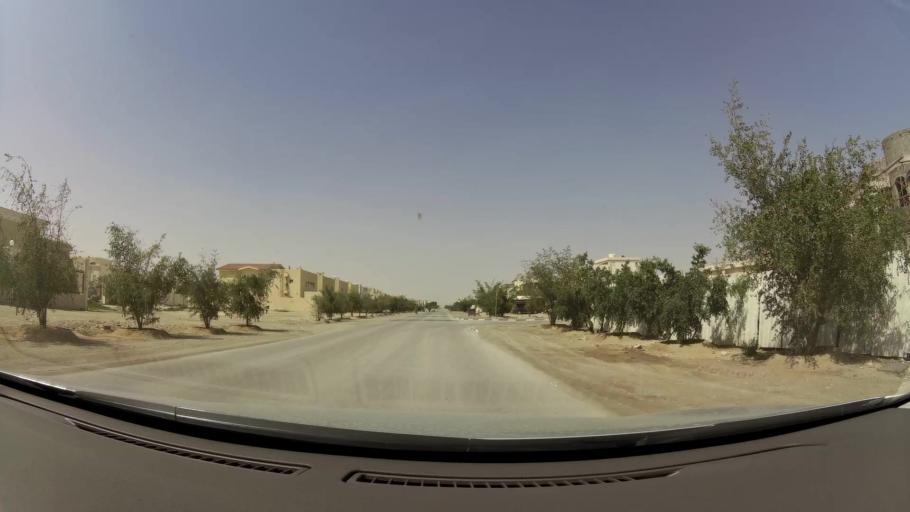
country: QA
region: Baladiyat Umm Salal
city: Umm Salal Muhammad
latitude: 25.3750
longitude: 51.4208
